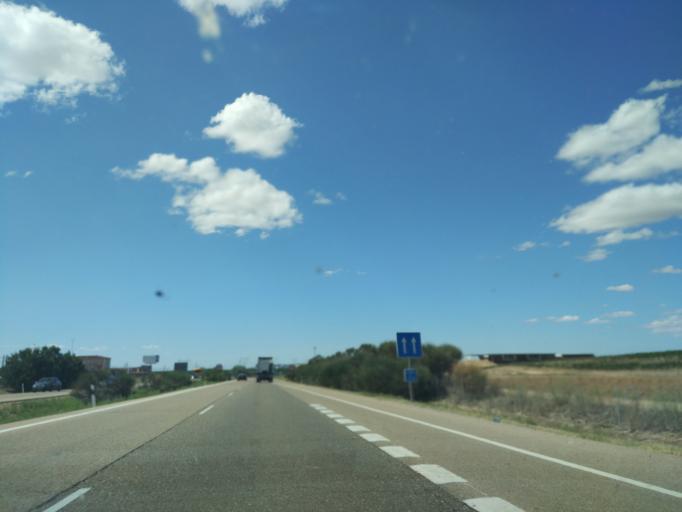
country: ES
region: Castille and Leon
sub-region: Provincia de Valladolid
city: Rueda
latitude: 41.4271
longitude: -4.9680
